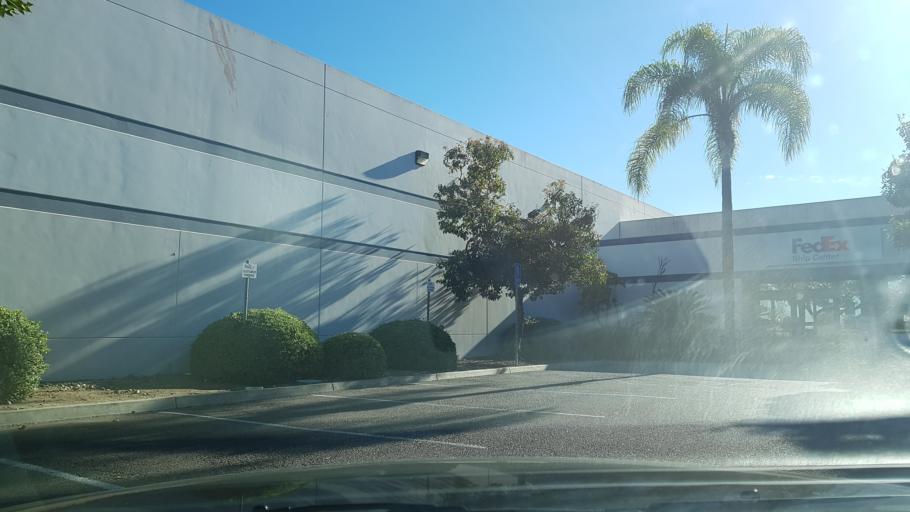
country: US
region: California
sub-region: San Diego County
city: Fairbanks Ranch
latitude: 32.9095
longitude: -117.1735
